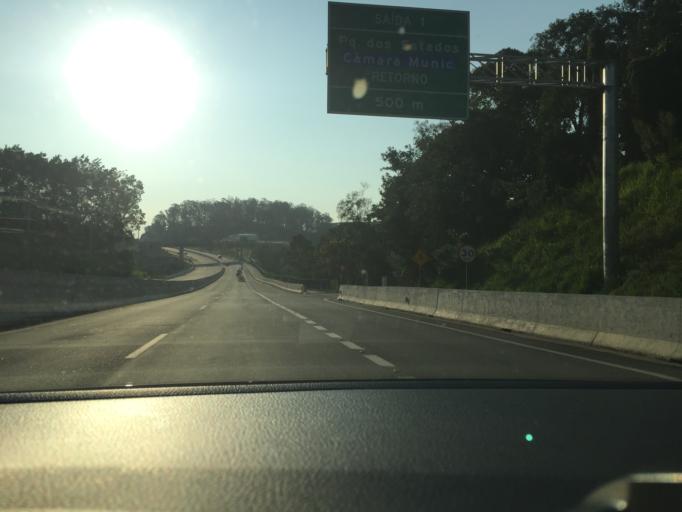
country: BR
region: Sao Paulo
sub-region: Louveira
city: Louveira
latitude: -23.0920
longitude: -46.9571
